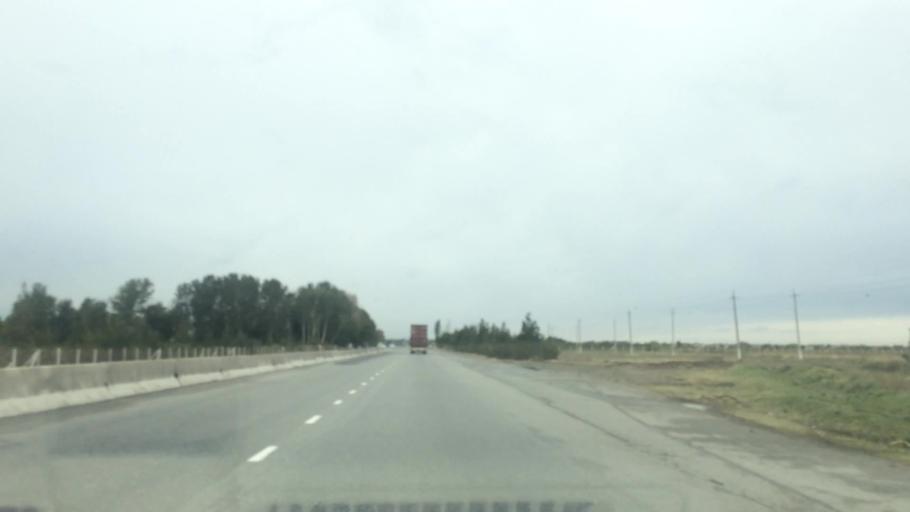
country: UZ
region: Samarqand
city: Bulung'ur
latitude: 39.7809
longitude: 67.2975
